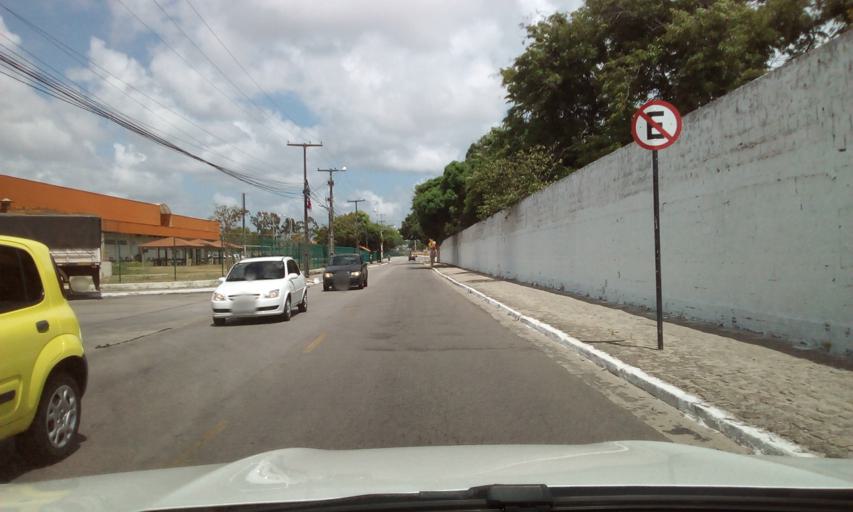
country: BR
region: Paraiba
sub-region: Joao Pessoa
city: Joao Pessoa
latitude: -7.1714
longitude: -34.8637
